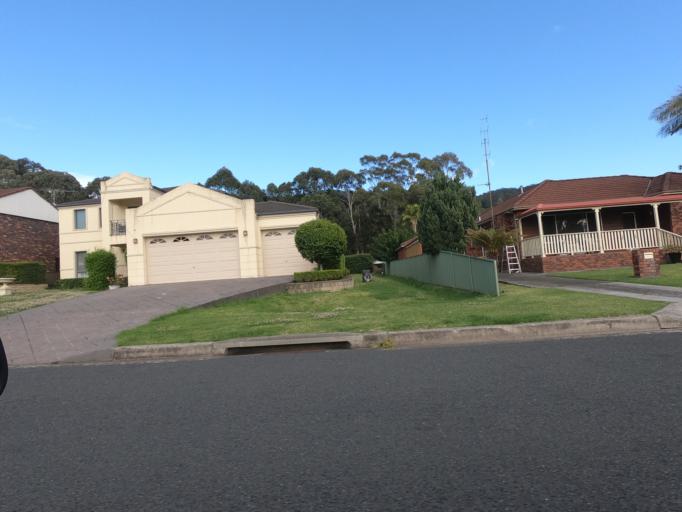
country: AU
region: New South Wales
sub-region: Wollongong
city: Corrimal
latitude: -34.3575
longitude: 150.8961
